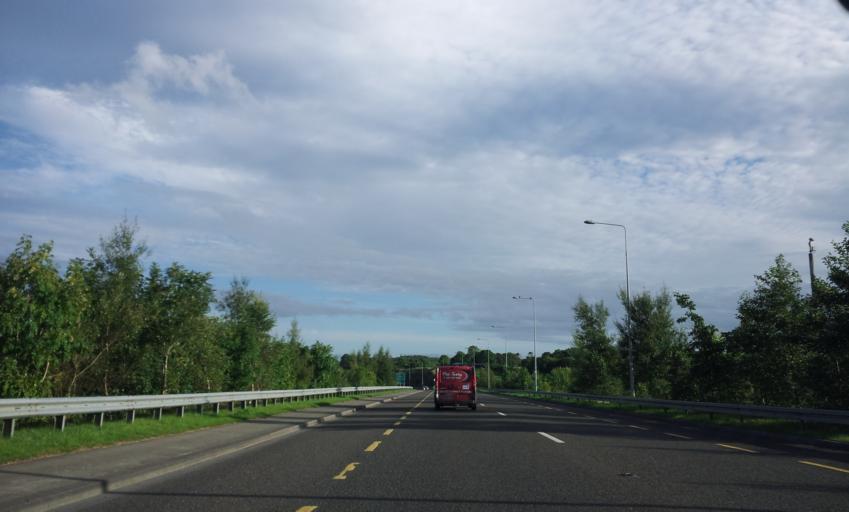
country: IE
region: Munster
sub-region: An Clar
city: Ennis
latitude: 52.8330
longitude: -9.0085
